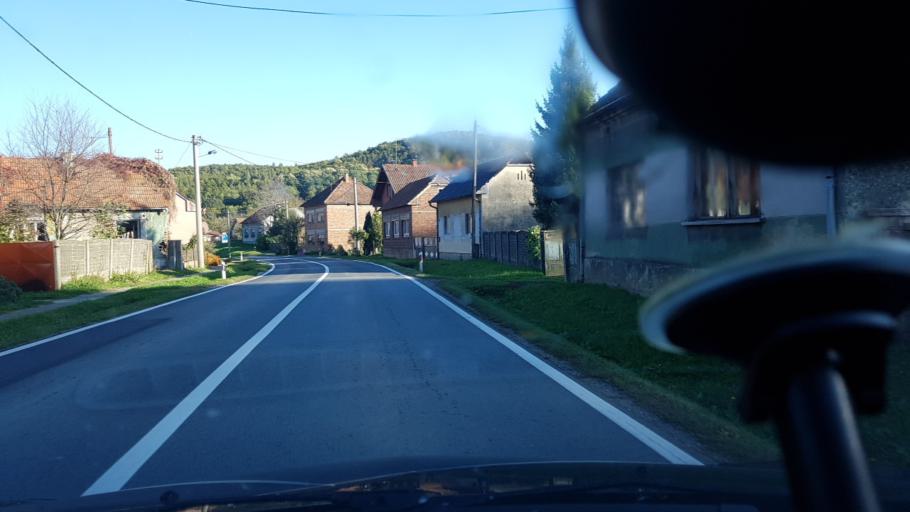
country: HR
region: Koprivnicko-Krizevacka
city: Virje
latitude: 46.0158
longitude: 16.9579
